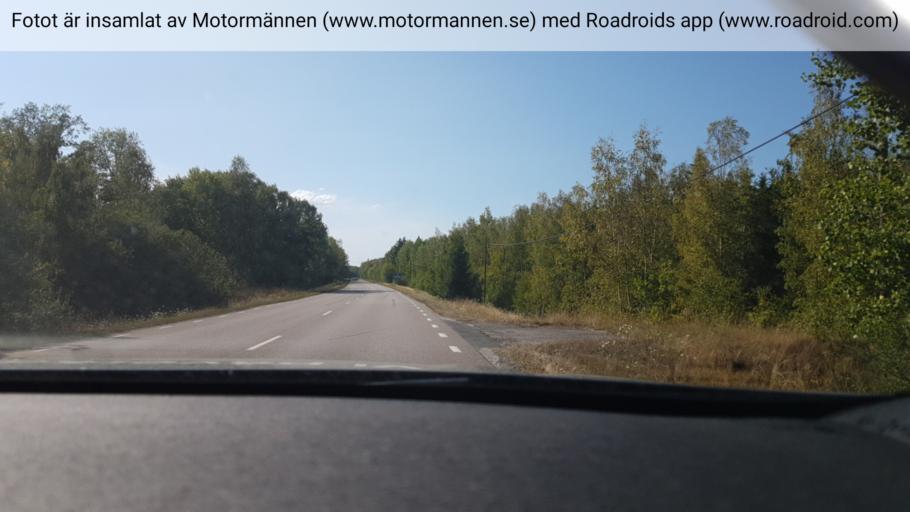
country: SE
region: Vaestra Goetaland
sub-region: Gotene Kommun
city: Goetene
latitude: 58.6250
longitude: 13.4682
